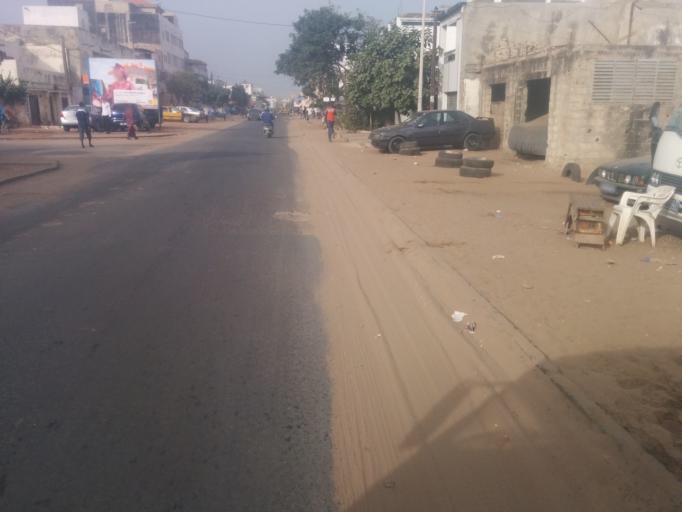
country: SN
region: Dakar
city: Grand Dakar
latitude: 14.7600
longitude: -17.4429
